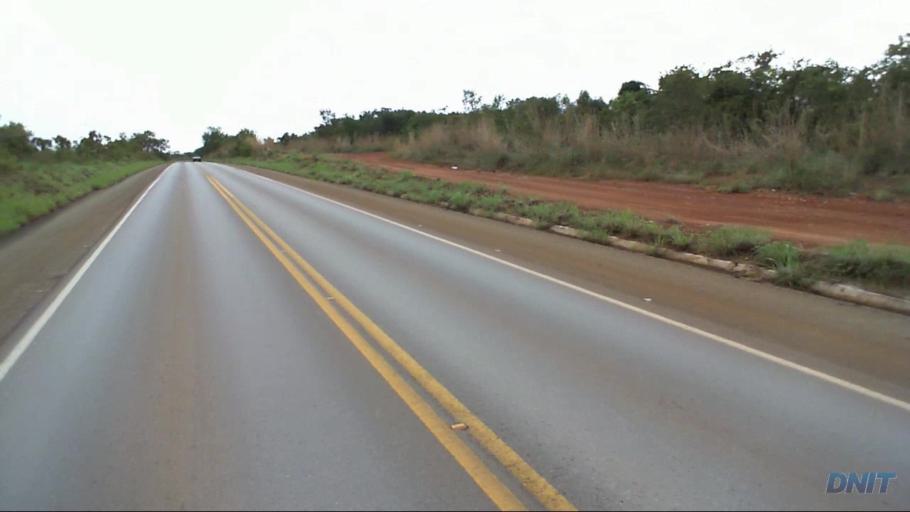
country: BR
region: Goias
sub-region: Barro Alto
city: Barro Alto
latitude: -14.7875
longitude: -49.0540
